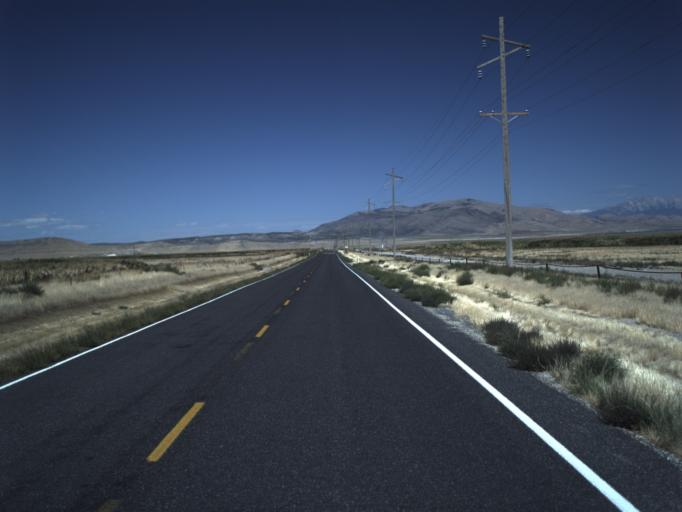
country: US
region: Utah
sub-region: Utah County
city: Genola
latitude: 40.0690
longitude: -111.9585
